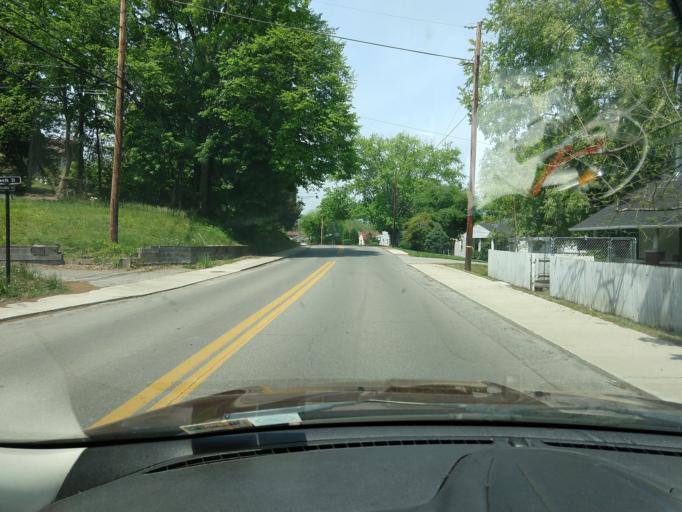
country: US
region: West Virginia
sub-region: Kanawha County
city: Saint Albans
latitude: 38.3820
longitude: -81.8271
